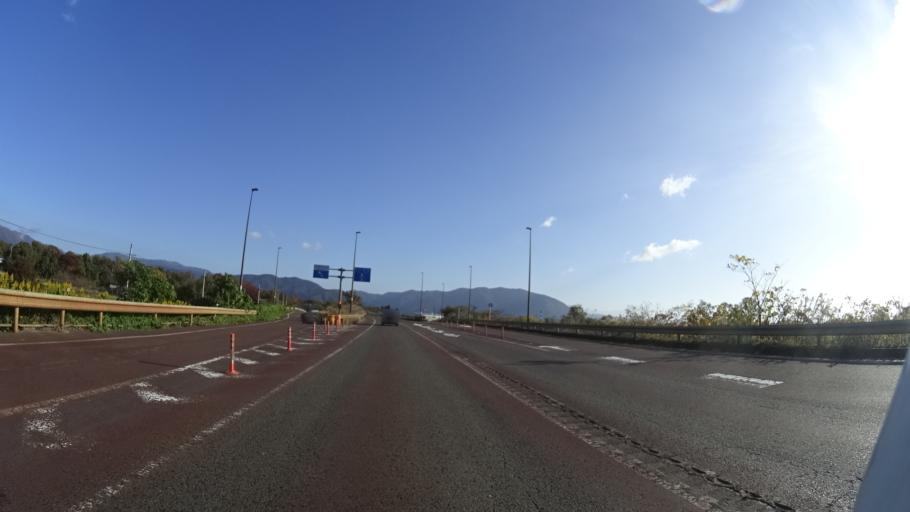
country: JP
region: Fukui
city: Tsuruga
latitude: 35.4404
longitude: 136.0258
